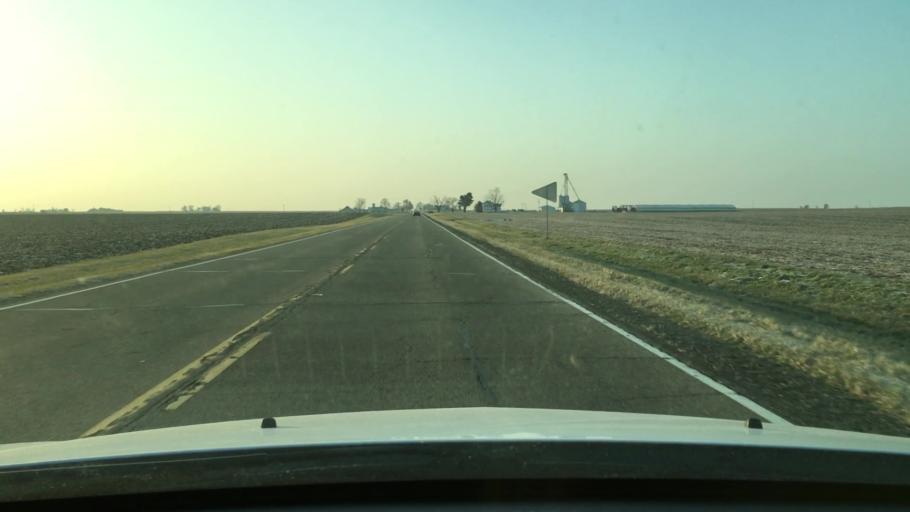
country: US
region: Illinois
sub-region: Putnam County
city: Granville
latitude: 41.2355
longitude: -89.2018
